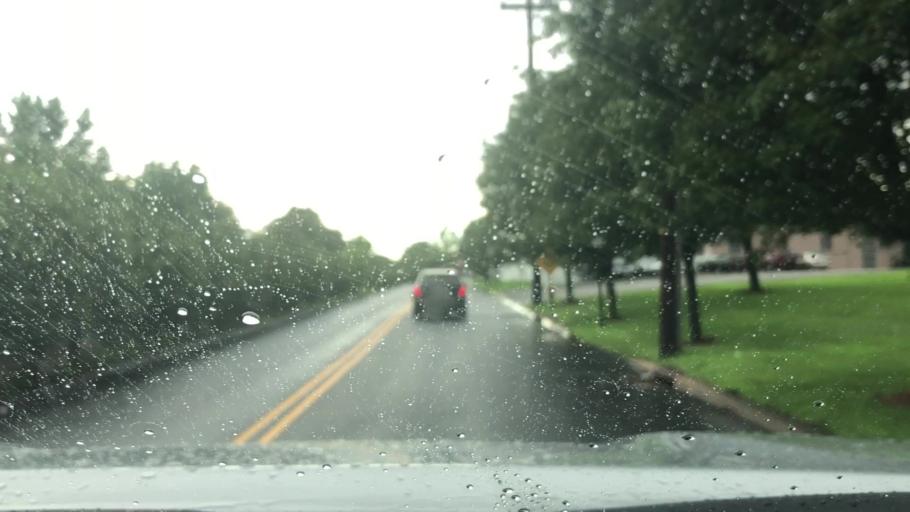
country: US
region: New Jersey
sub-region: Bergen County
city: Lodi
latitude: 40.8832
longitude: -74.0728
